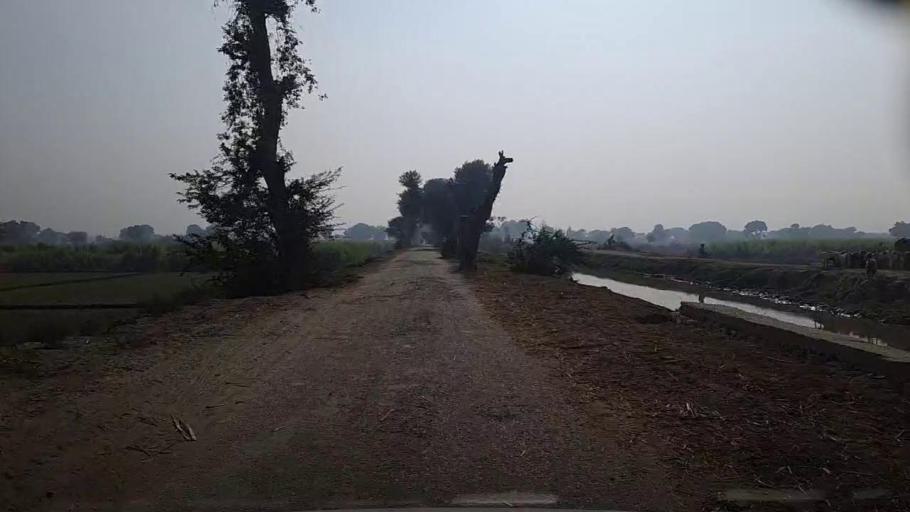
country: PK
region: Sindh
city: Setharja Old
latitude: 27.1165
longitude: 68.5097
